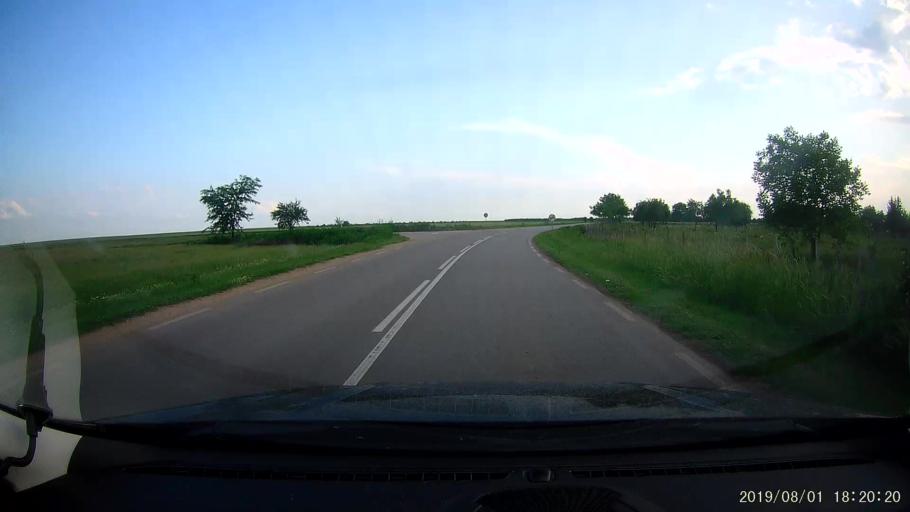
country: BG
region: Shumen
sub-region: Obshtina Kaolinovo
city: Kaolinovo
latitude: 43.6731
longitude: 27.0895
